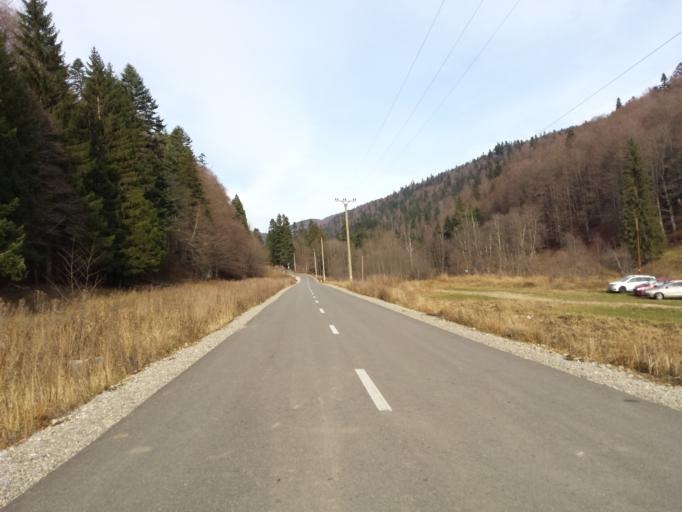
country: RO
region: Prahova
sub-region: Oras Azuga
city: Azuga
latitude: 45.4321
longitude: 25.5309
